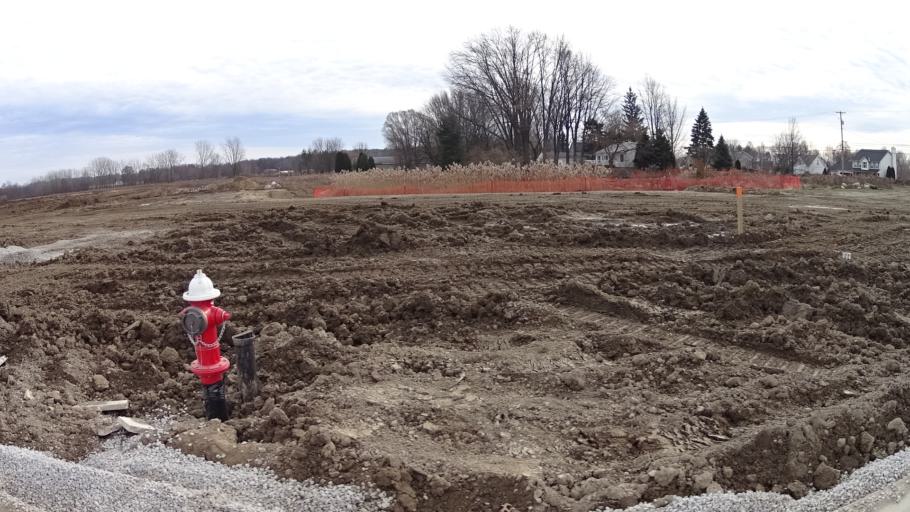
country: US
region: Ohio
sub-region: Lorain County
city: North Ridgeville
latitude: 41.4028
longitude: -82.0309
